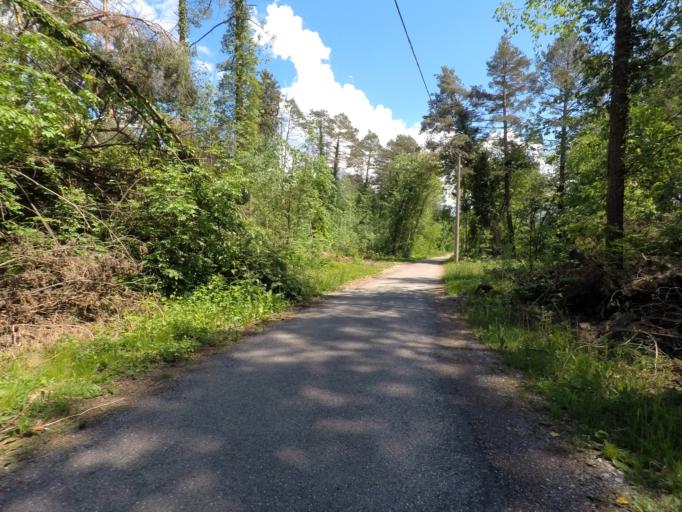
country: IT
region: Friuli Venezia Giulia
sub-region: Provincia di Udine
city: Chiaulis
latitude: 46.4040
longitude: 12.9884
